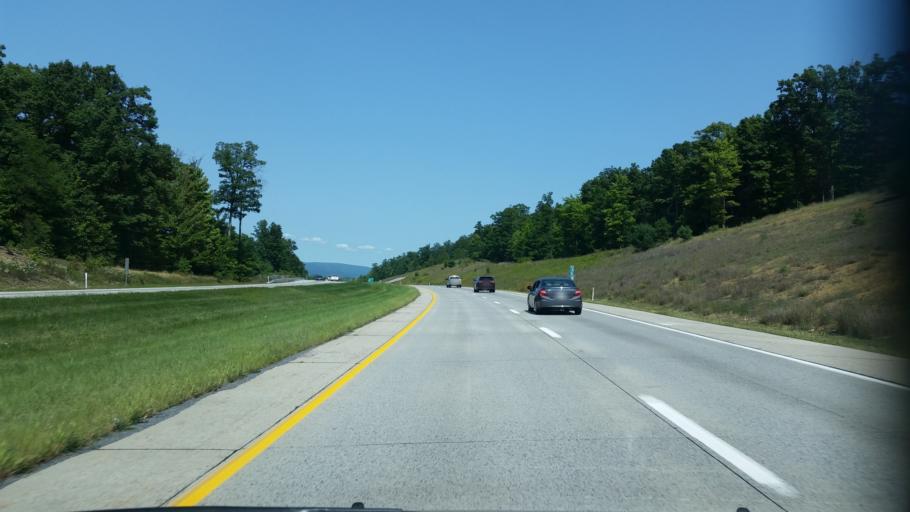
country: US
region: Pennsylvania
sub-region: Blair County
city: Greenwood
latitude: 40.5270
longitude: -78.3526
